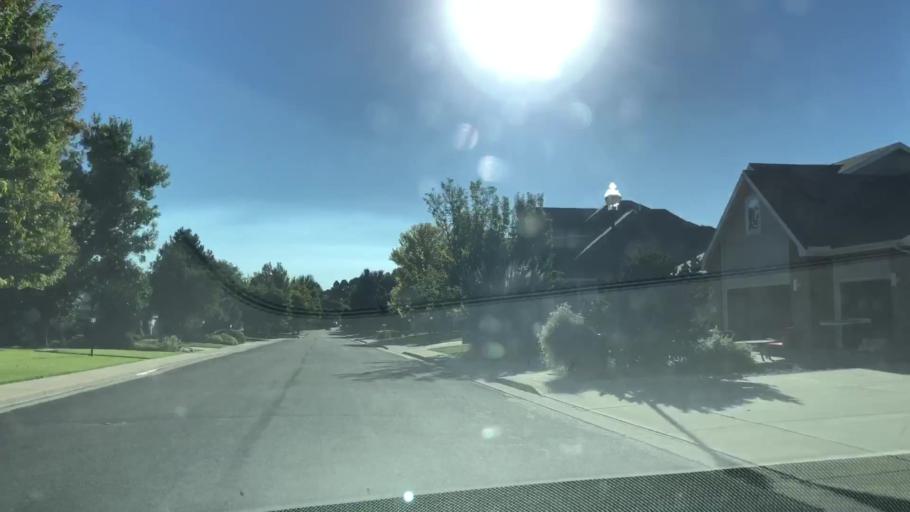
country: US
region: Colorado
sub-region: Larimer County
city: Loveland
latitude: 40.3994
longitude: -105.1467
